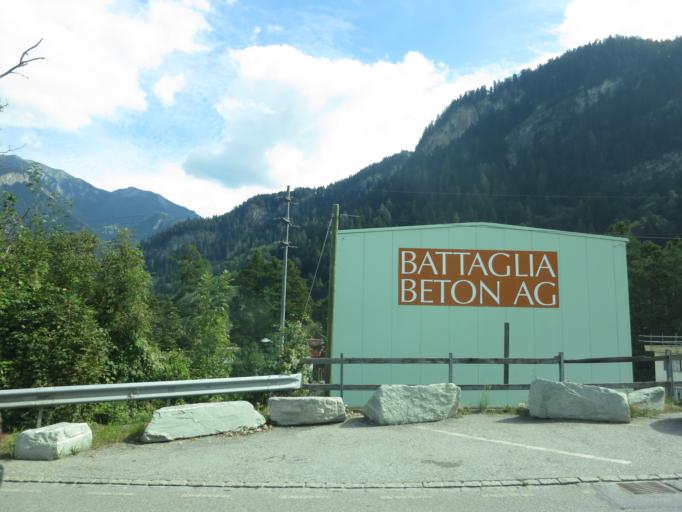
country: CH
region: Grisons
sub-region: Hinterrhein District
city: Thusis
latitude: 46.6965
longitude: 9.4422
